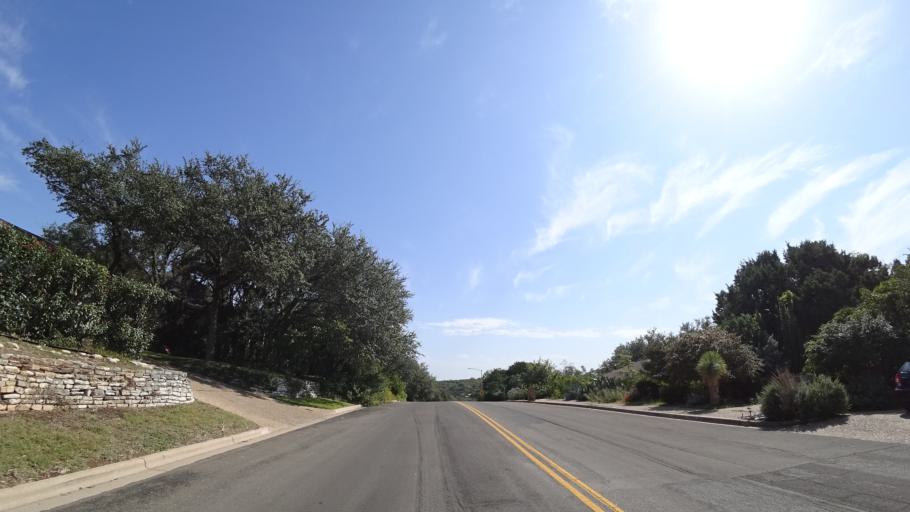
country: US
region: Texas
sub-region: Travis County
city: West Lake Hills
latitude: 30.3459
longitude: -97.7688
